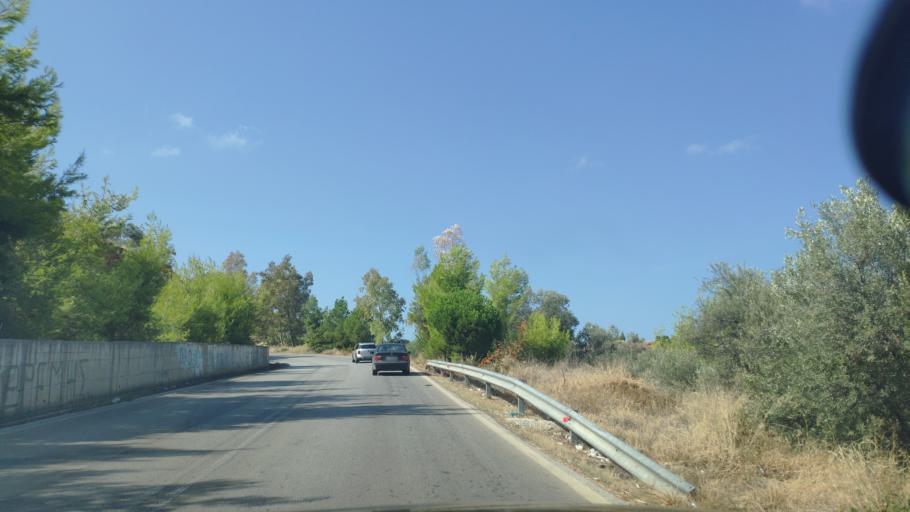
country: GR
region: Peloponnese
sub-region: Nomos Korinthias
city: Moulki
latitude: 37.9996
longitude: 22.7130
